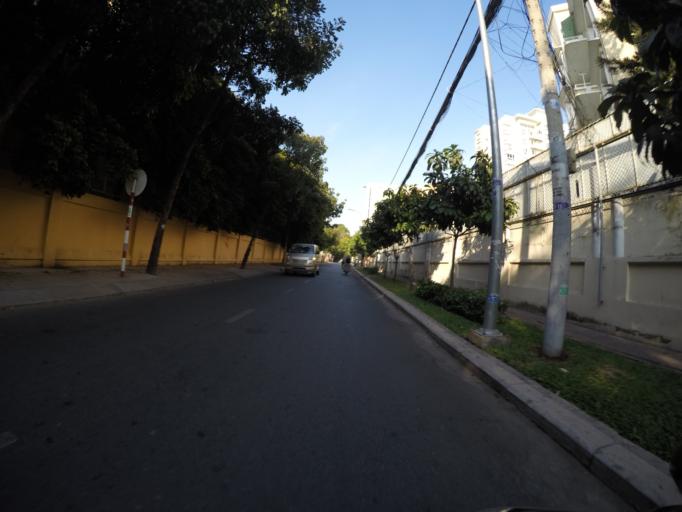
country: VN
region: Ho Chi Minh City
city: Quan Ba
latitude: 10.7783
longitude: 106.6876
